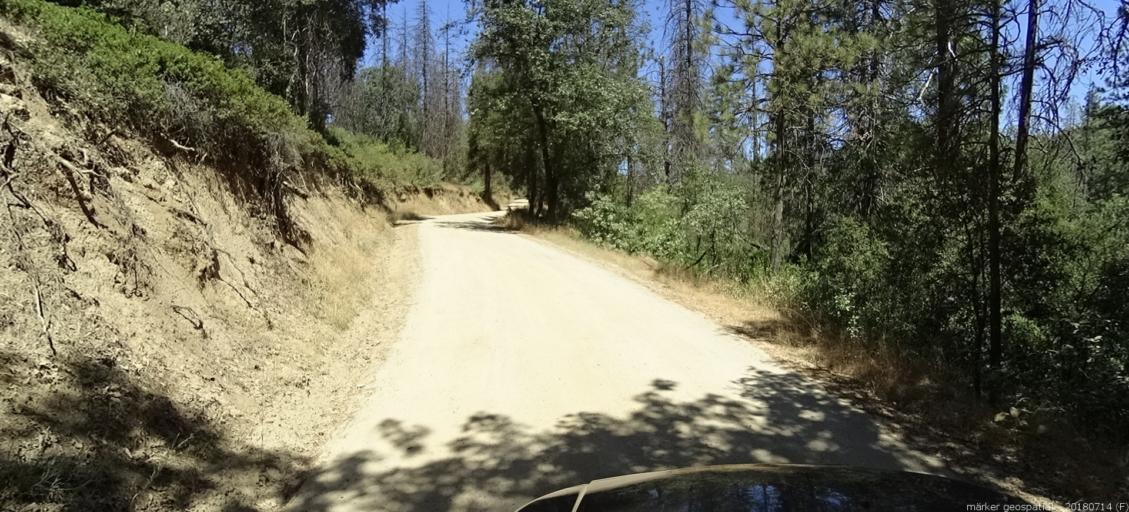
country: US
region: California
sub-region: Madera County
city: Ahwahnee
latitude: 37.3929
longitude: -119.6895
